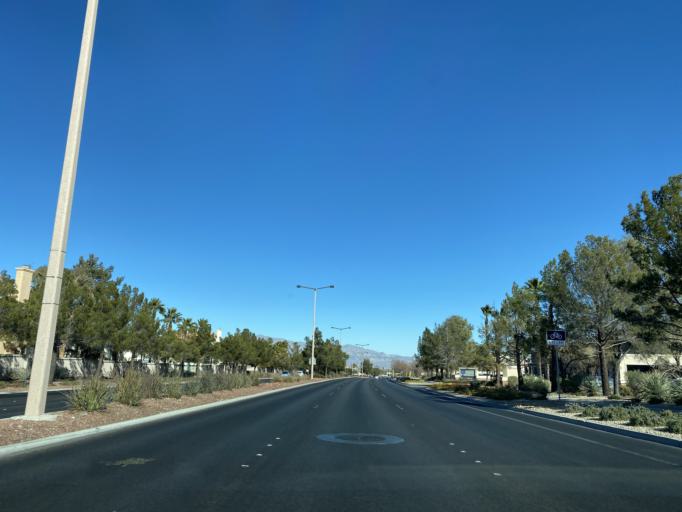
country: US
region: Nevada
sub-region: Clark County
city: Summerlin South
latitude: 36.1970
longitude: -115.2849
